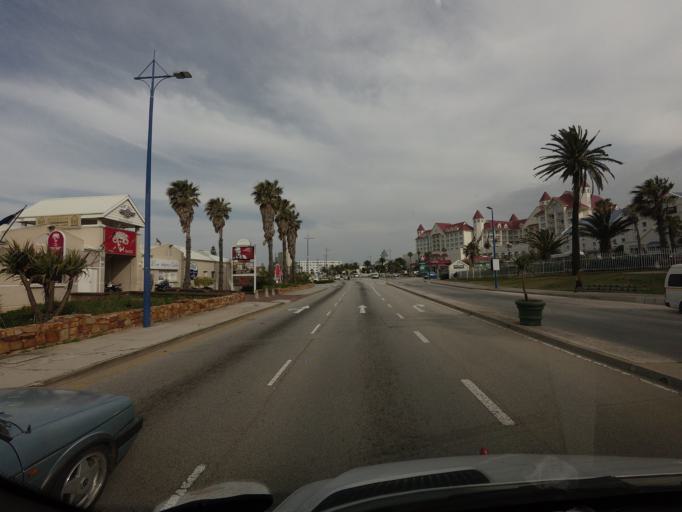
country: ZA
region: Eastern Cape
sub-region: Nelson Mandela Bay Metropolitan Municipality
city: Port Elizabeth
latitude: -33.9803
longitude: 25.6566
